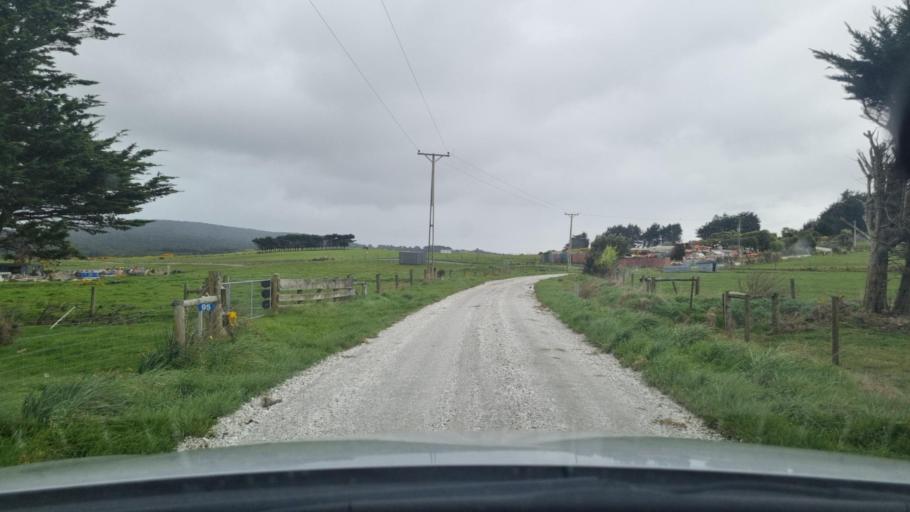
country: NZ
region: Southland
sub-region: Invercargill City
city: Bluff
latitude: -46.5408
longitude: 168.2911
